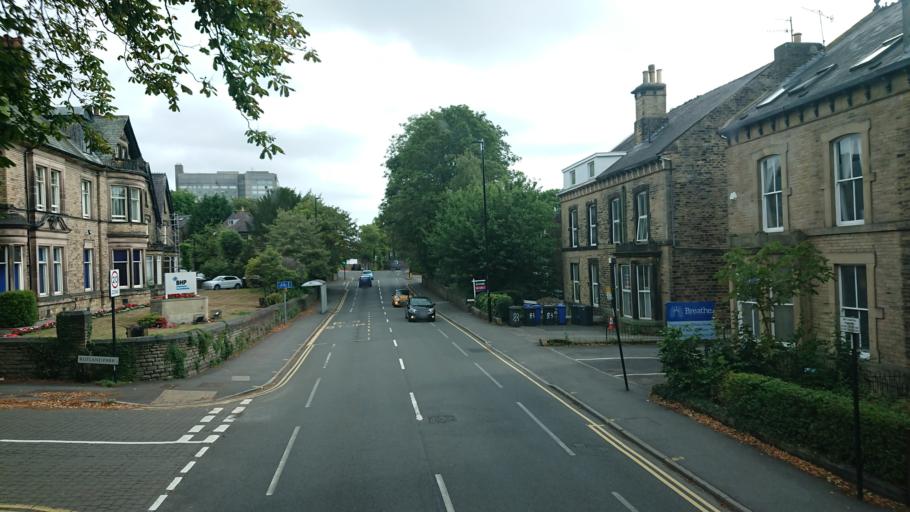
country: GB
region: England
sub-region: Sheffield
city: Sheffield
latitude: 53.3741
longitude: -1.4973
